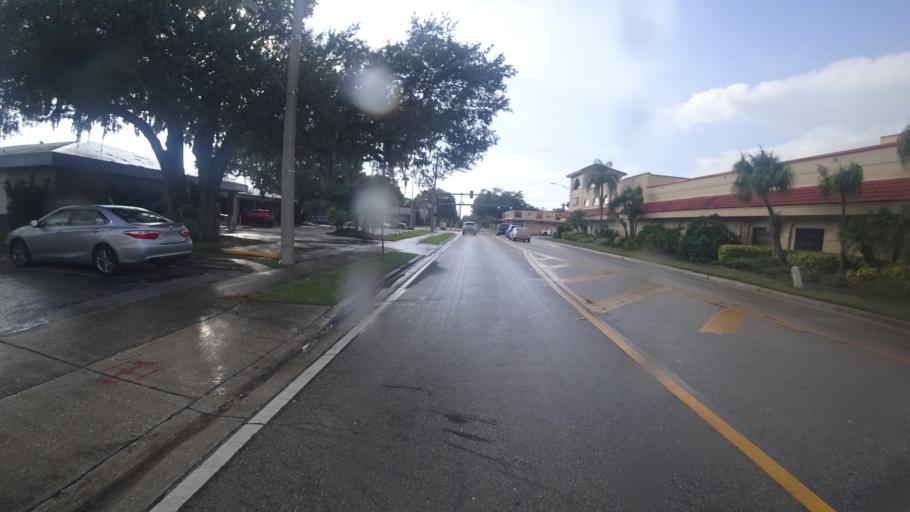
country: US
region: Florida
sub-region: Manatee County
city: Palmetto
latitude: 27.5175
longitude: -82.5723
